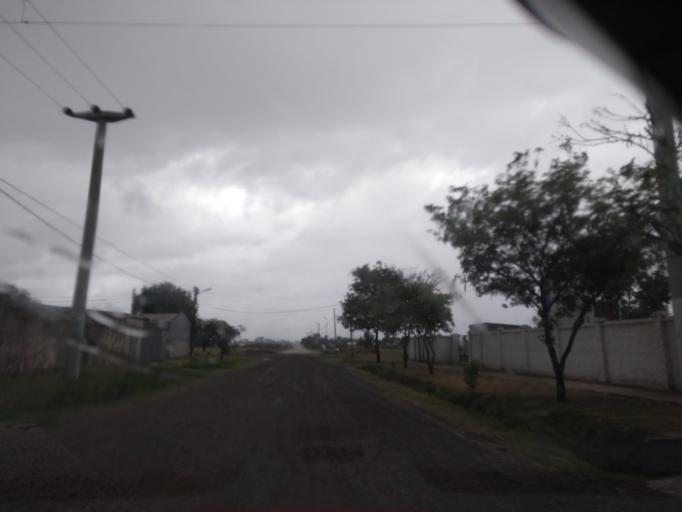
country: AR
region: Chaco
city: Fontana
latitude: -27.4225
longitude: -59.0466
